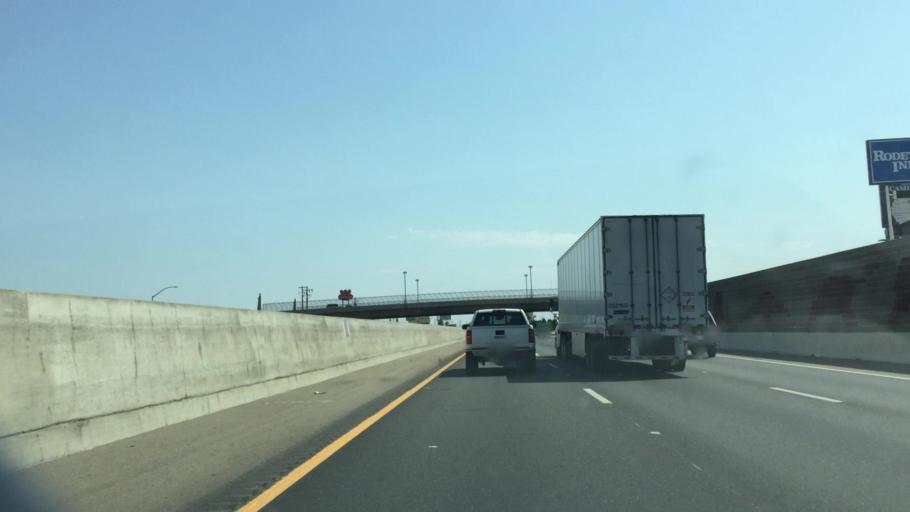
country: US
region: California
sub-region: San Joaquin County
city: Morada
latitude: 38.0232
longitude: -121.2583
